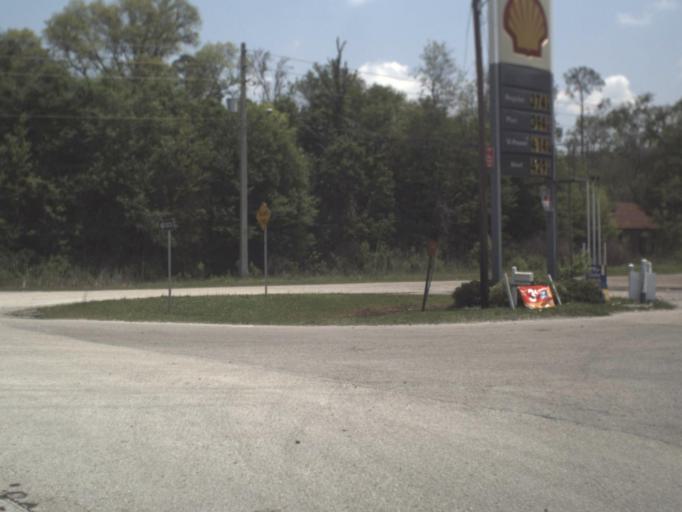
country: US
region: Florida
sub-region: Duval County
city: Baldwin
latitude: 30.2031
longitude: -82.0140
